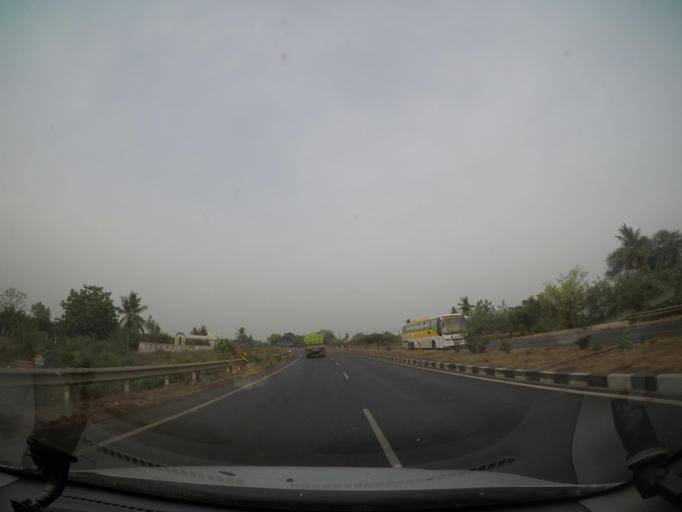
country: IN
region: Andhra Pradesh
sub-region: Krishna
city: Gannavaram
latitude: 16.6164
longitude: 80.9251
